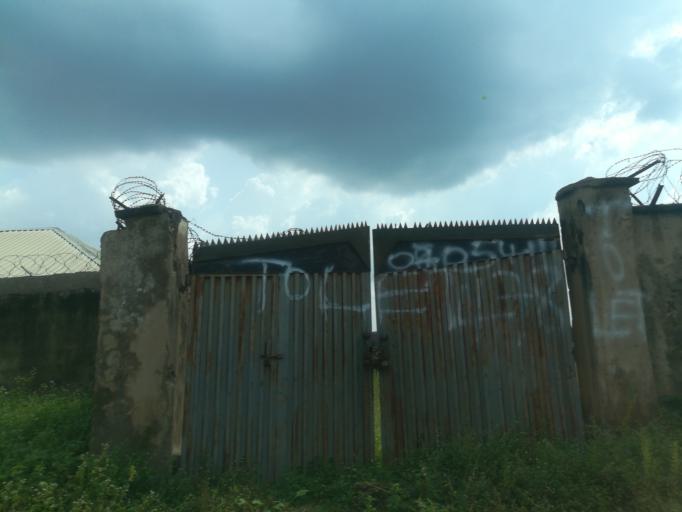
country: NG
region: Oyo
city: Moniya
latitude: 7.4648
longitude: 3.9180
